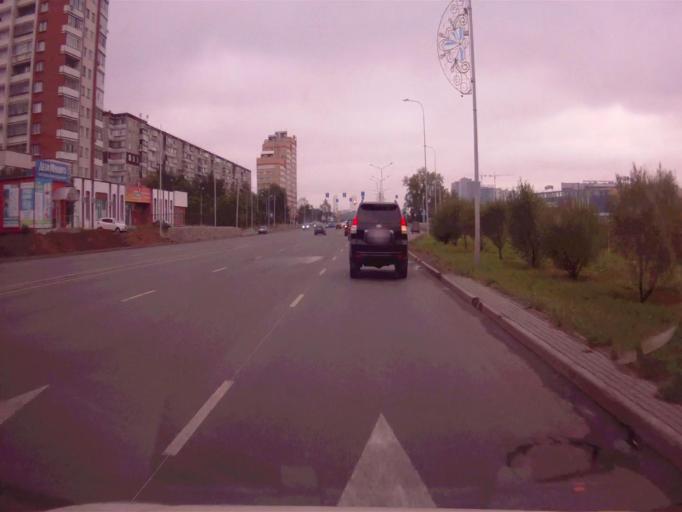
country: RU
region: Chelyabinsk
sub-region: Gorod Chelyabinsk
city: Chelyabinsk
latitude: 55.1736
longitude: 61.3493
